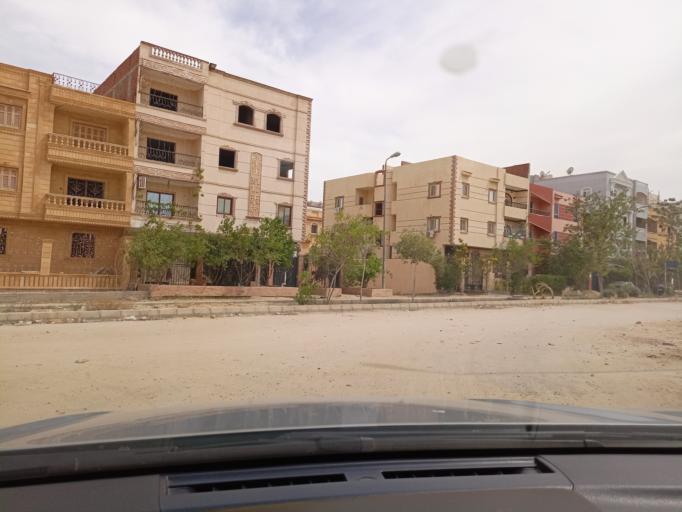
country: EG
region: Muhafazat al Qalyubiyah
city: Al Khankah
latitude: 30.2480
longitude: 31.4994
